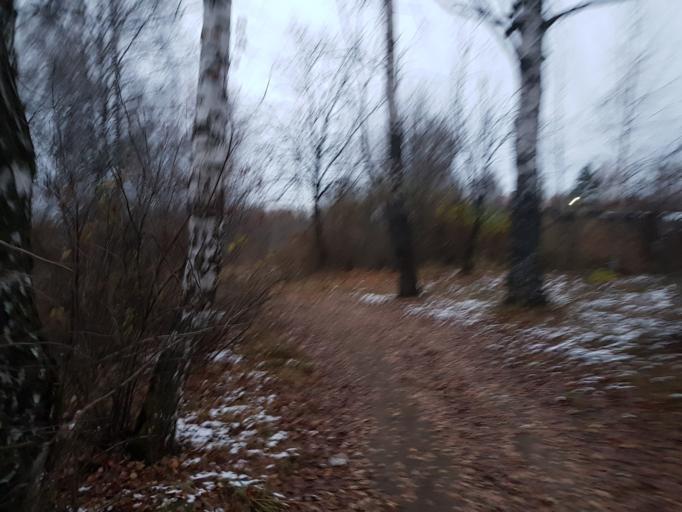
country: RU
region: Moskovskaya
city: Istra
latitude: 55.9026
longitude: 36.8683
